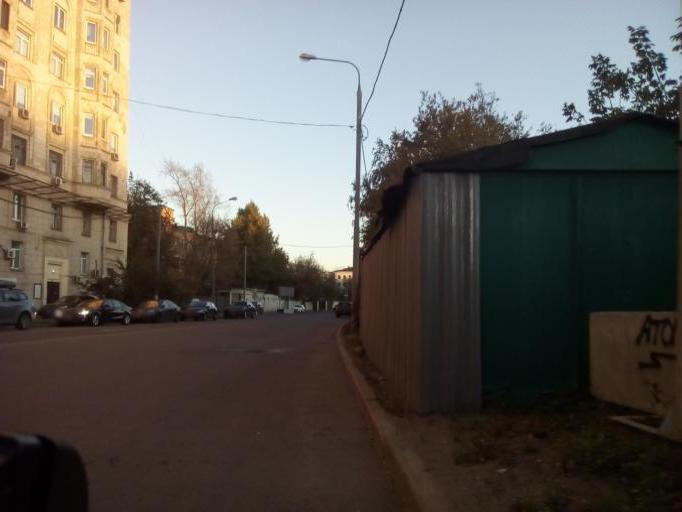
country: RU
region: Moskovskaya
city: Koptevo
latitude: 55.8085
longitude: 37.4914
